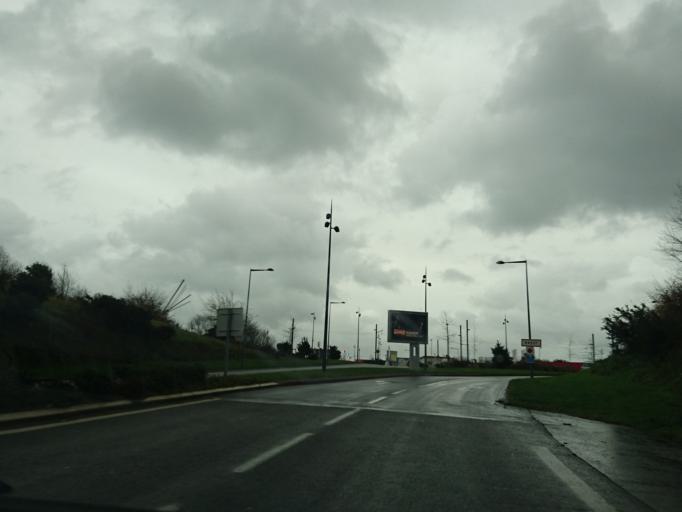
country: FR
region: Brittany
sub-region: Departement du Finistere
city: Guilers
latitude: 48.3791
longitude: -4.5456
